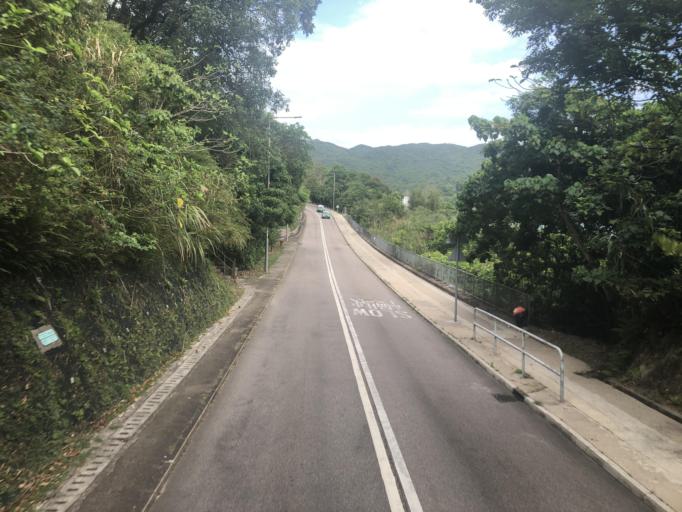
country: HK
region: Sai Kung
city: Sai Kung
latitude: 22.3933
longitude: 114.3118
